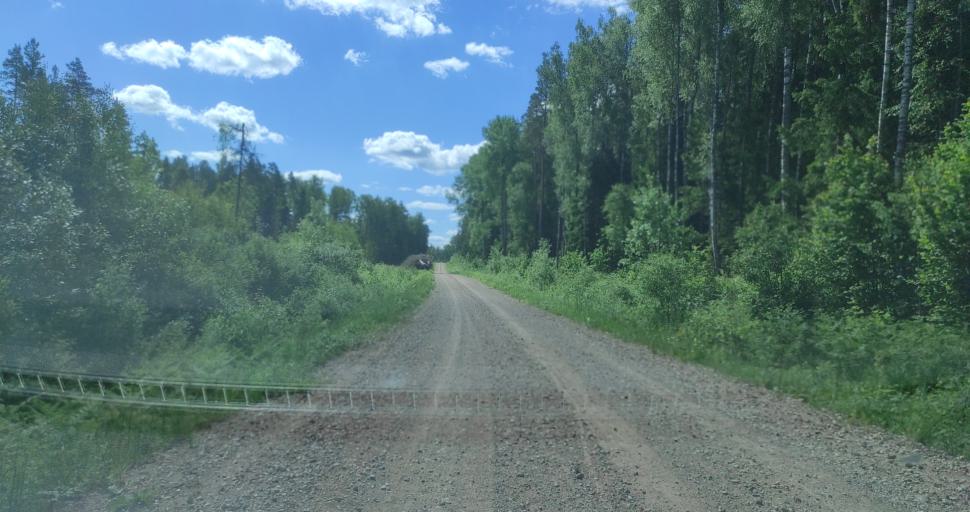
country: LV
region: Kuldigas Rajons
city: Kuldiga
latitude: 56.9405
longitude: 21.7903
